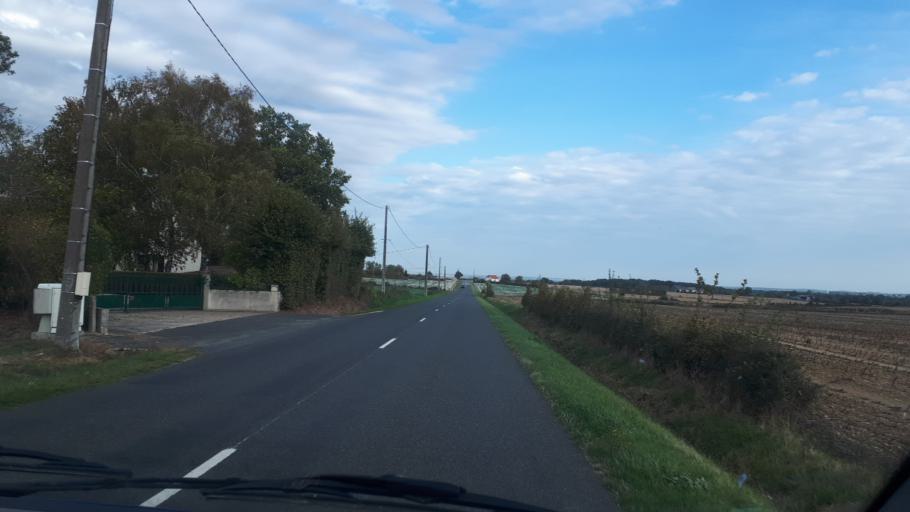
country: FR
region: Centre
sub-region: Departement du Loir-et-Cher
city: Mondoubleau
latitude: 47.9518
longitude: 0.9318
